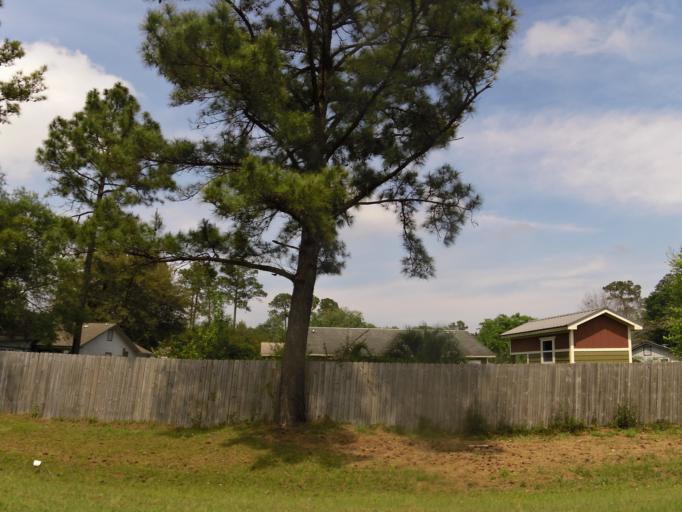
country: US
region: Georgia
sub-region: Camden County
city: Kingsland
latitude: 30.7737
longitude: -81.6734
